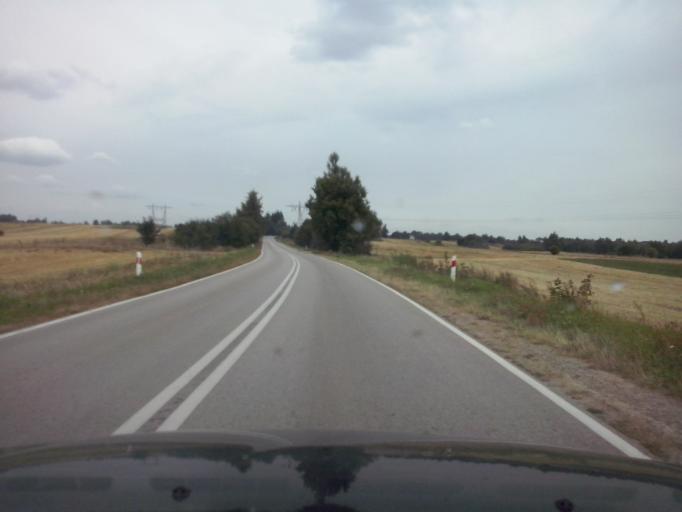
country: PL
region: Swietokrzyskie
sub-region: Powiat kielecki
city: Lagow
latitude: 50.7245
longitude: 21.0663
